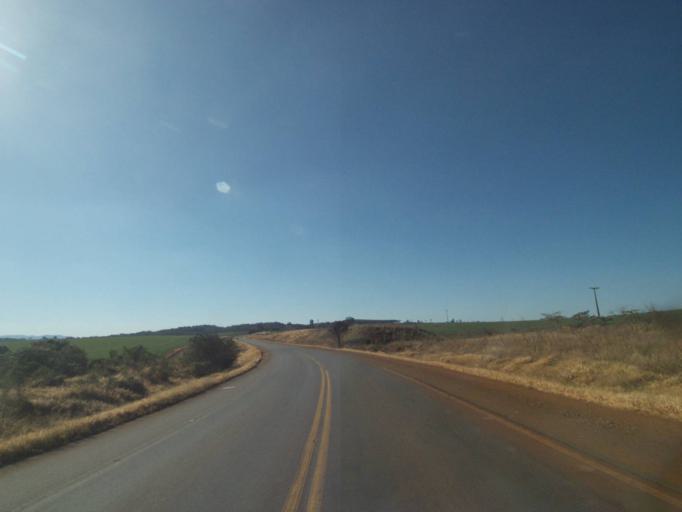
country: BR
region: Parana
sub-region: Tibagi
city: Tibagi
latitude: -24.7467
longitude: -50.4614
